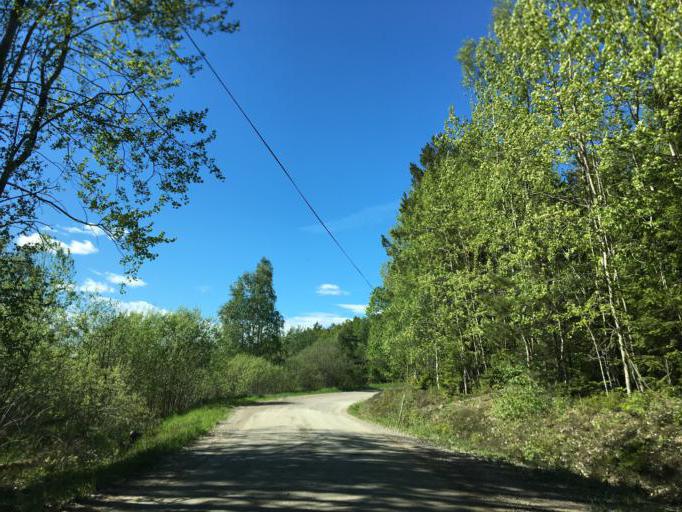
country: SE
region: Soedermanland
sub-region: Eskilstuna Kommun
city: Kvicksund
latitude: 59.3582
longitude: 16.2619
